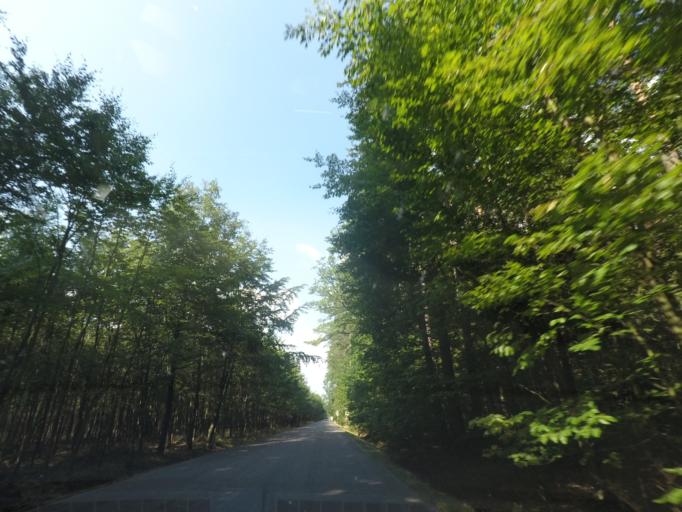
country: CZ
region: Pardubicky
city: Horni Jeleni
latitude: 50.0621
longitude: 16.0823
